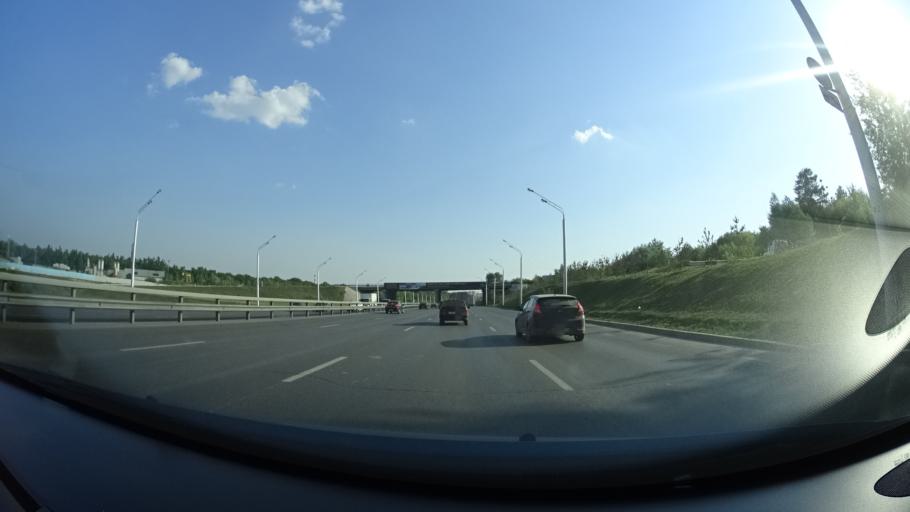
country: RU
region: Bashkortostan
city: Ufa
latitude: 54.7400
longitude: 56.0081
